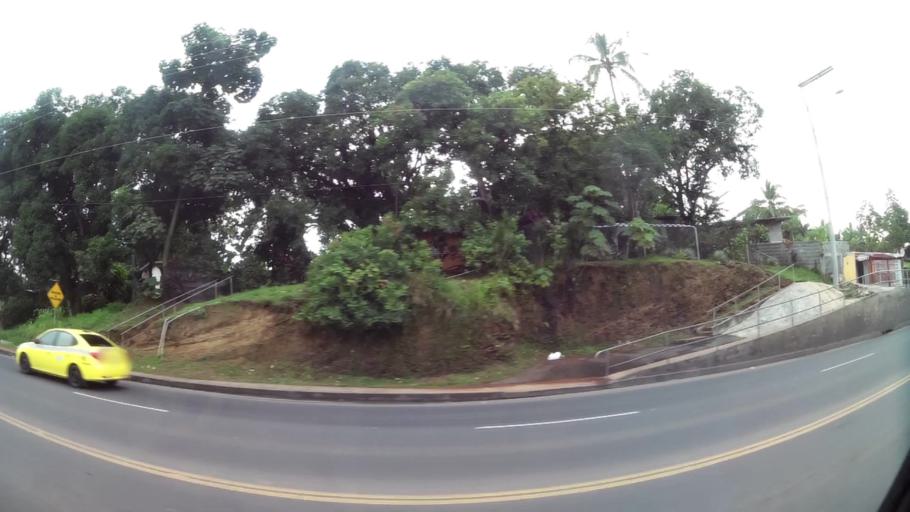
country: PA
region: Panama
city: Tocumen
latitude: 9.0958
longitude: -79.3689
